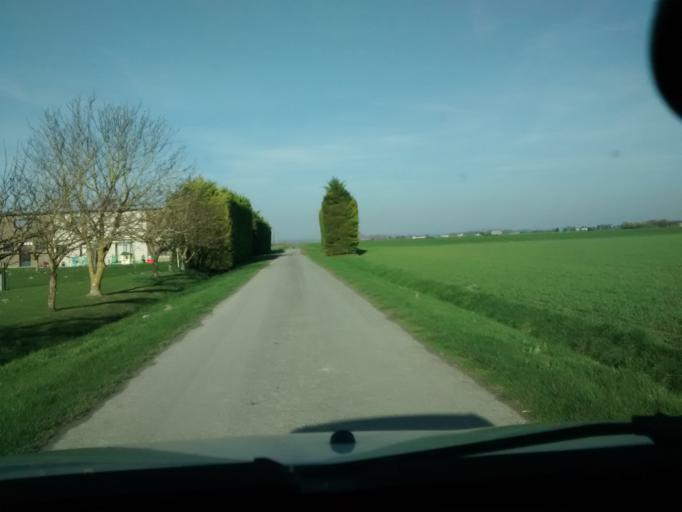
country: FR
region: Lower Normandy
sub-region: Departement de la Manche
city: Pontorson
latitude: 48.5882
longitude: -1.5261
